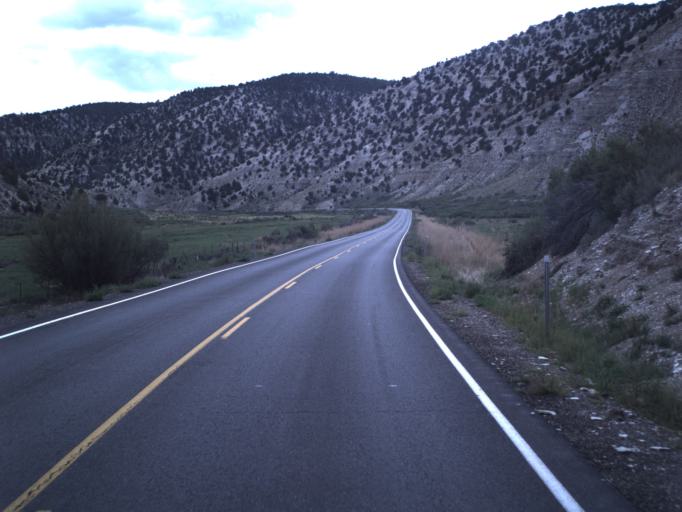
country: US
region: Utah
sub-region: Duchesne County
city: Duchesne
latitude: 40.0788
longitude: -110.5028
